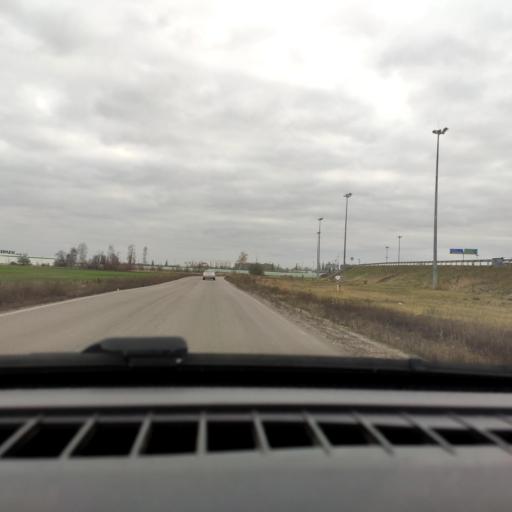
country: RU
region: Voronezj
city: Novaya Usman'
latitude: 51.6555
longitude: 39.3038
